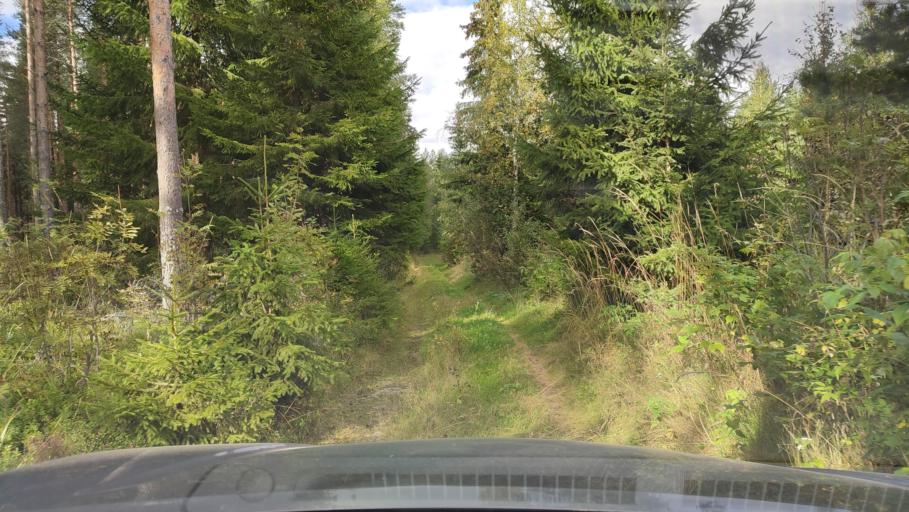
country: FI
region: Southern Ostrobothnia
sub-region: Suupohja
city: Karijoki
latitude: 62.2212
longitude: 21.6195
